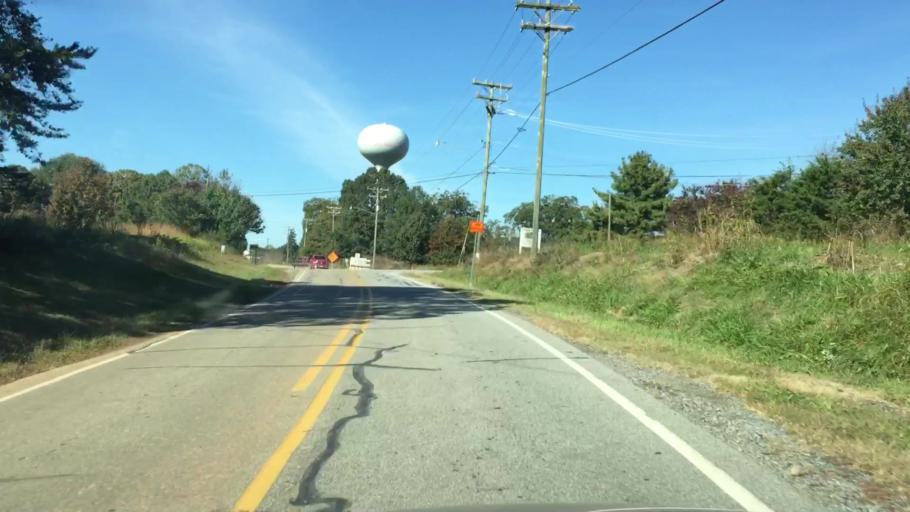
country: US
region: North Carolina
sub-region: Rockingham County
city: Reidsville
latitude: 36.3258
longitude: -79.6358
